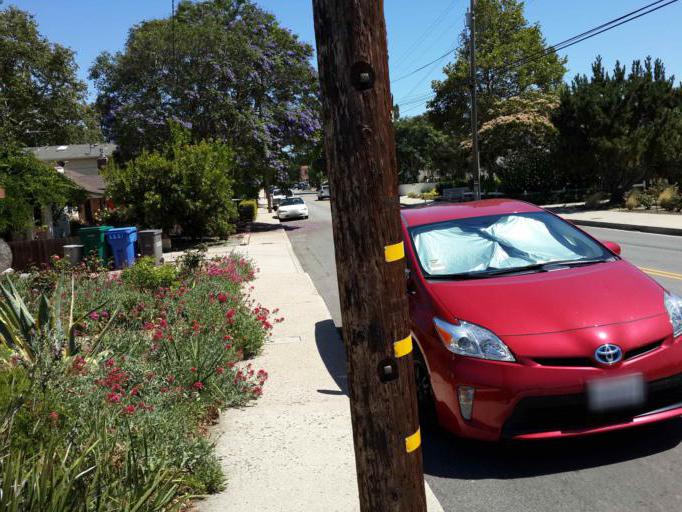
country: US
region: California
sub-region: San Luis Obispo County
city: San Luis Obispo
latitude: 35.2862
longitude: -120.6699
